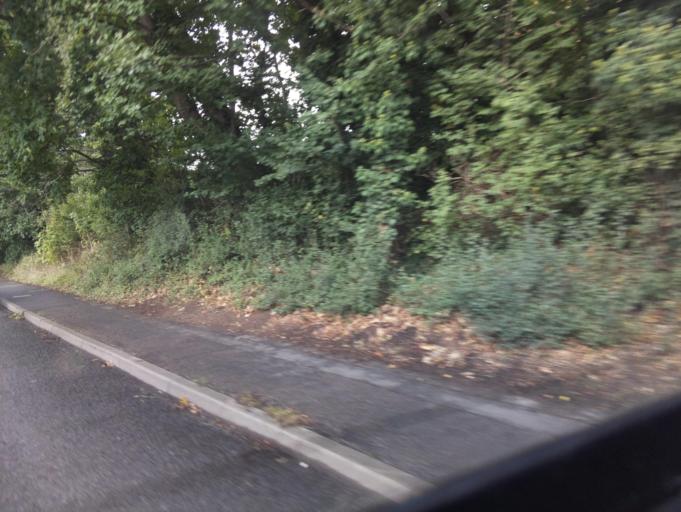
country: GB
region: England
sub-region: Worcestershire
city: Kidderminster
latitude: 52.3788
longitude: -2.2273
